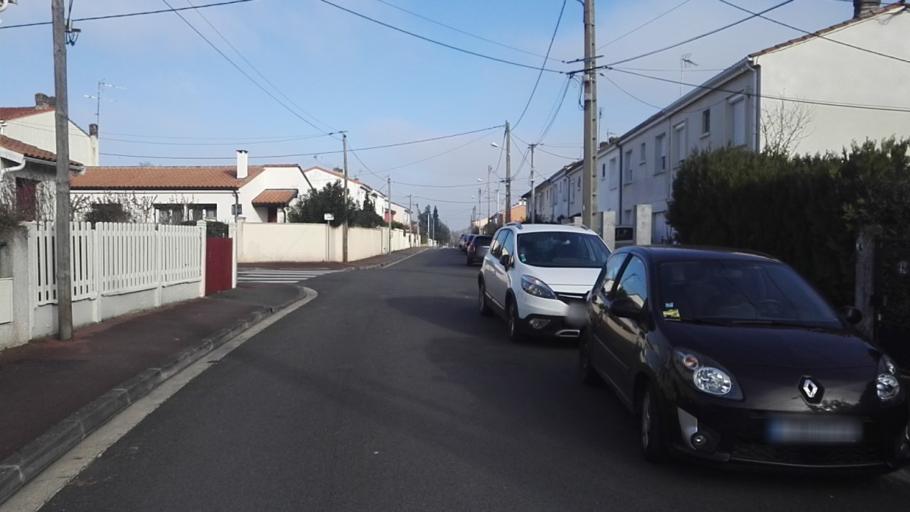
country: FR
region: Aquitaine
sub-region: Departement de la Gironde
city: Talence
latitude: 44.8028
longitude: -0.5841
